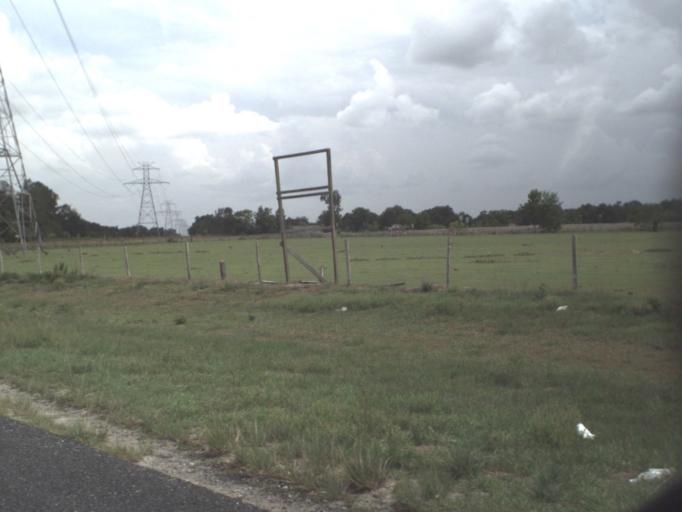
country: US
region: Florida
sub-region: Marion County
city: Belleview
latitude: 29.0322
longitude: -82.0243
